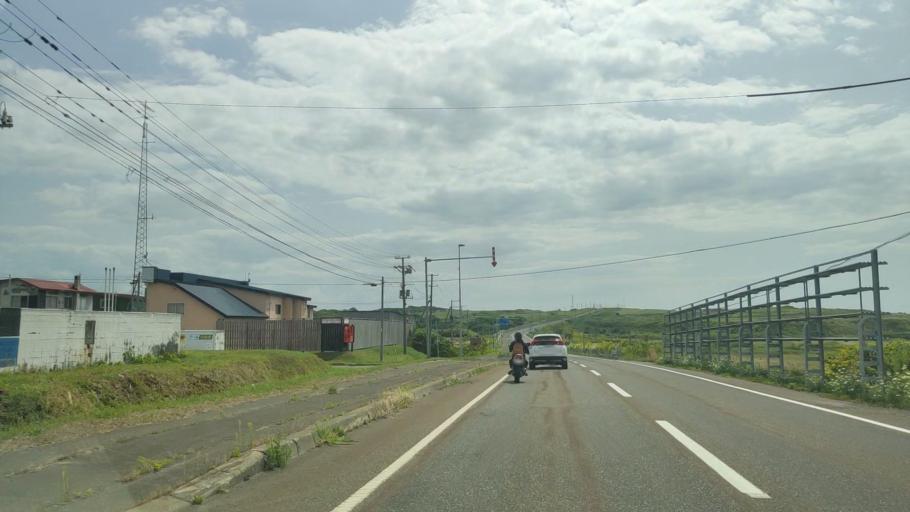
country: JP
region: Hokkaido
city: Rumoi
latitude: 44.4501
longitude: 141.7576
